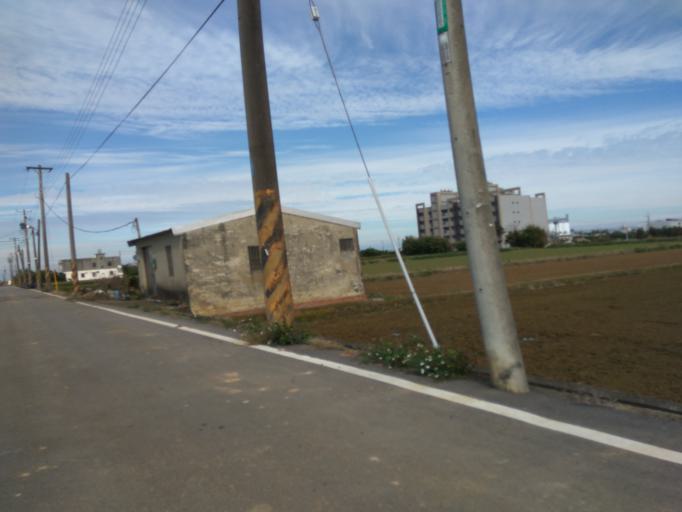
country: TW
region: Taiwan
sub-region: Hsinchu
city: Zhubei
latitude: 24.9886
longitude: 121.0920
